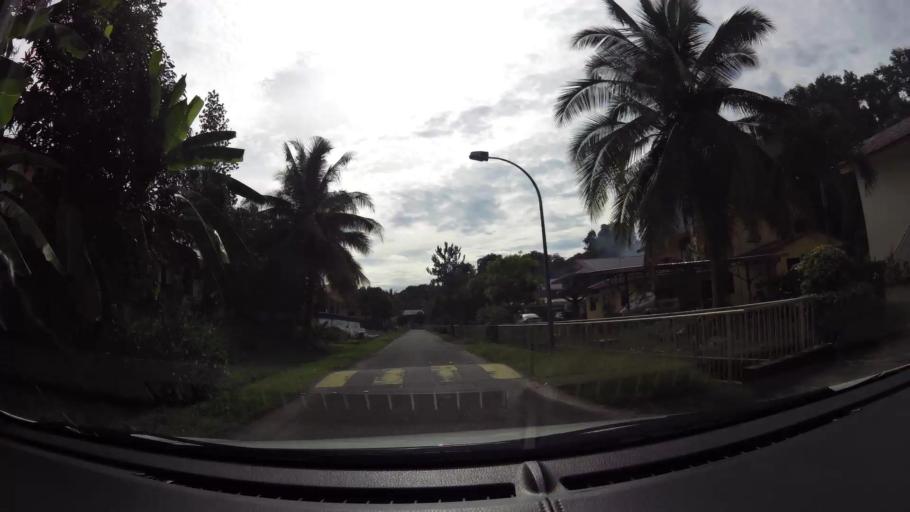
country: BN
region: Brunei and Muara
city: Bandar Seri Begawan
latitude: 4.8962
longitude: 114.8887
